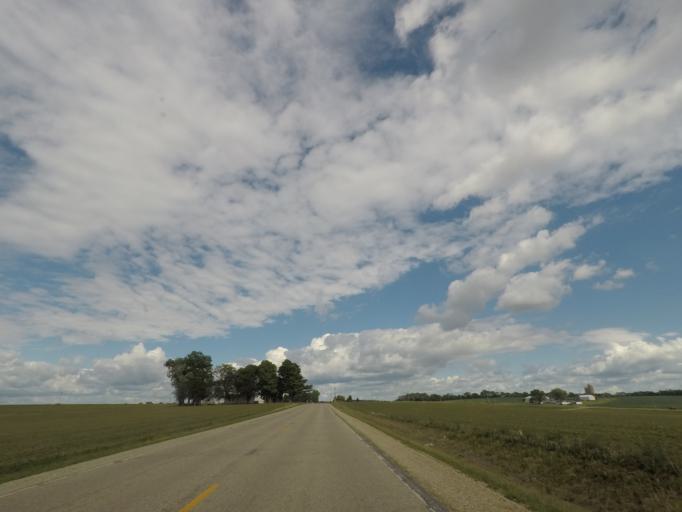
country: US
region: Wisconsin
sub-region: Rock County
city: Orfordville
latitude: 42.7043
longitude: -89.1545
